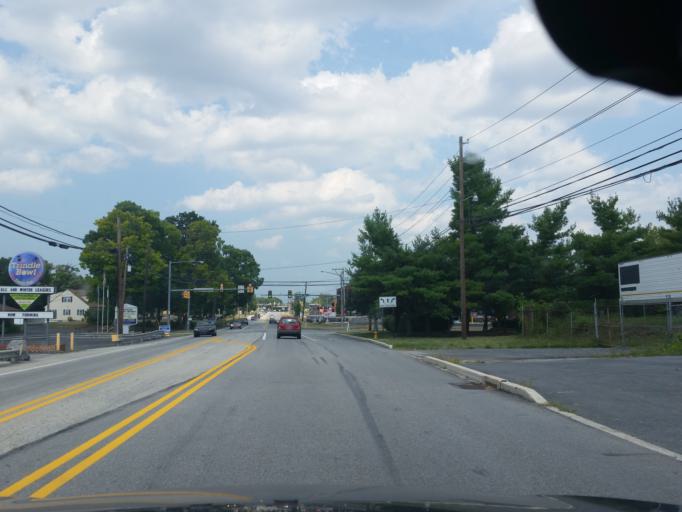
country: US
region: Pennsylvania
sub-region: Cumberland County
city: Shiremanstown
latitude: 40.2292
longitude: -76.9608
